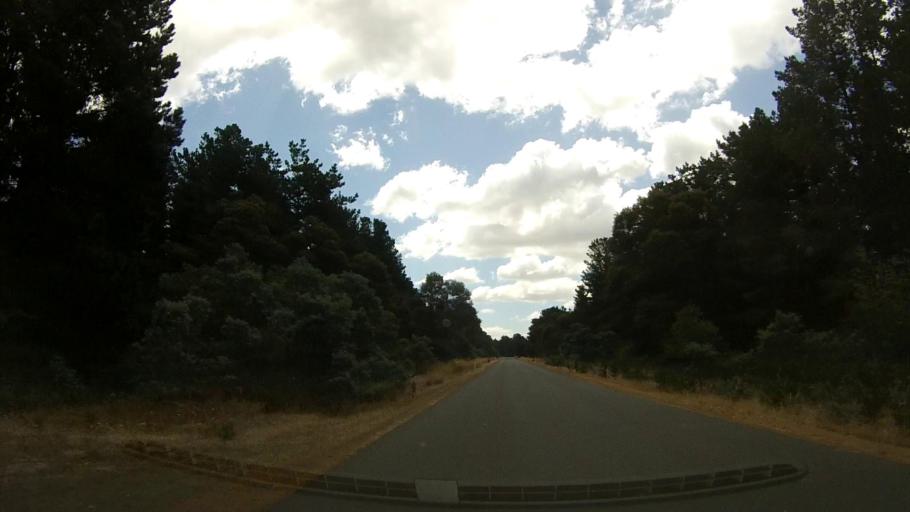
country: AU
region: Tasmania
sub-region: Clarence
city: Seven Mile Beach
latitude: -42.8398
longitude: 147.5300
